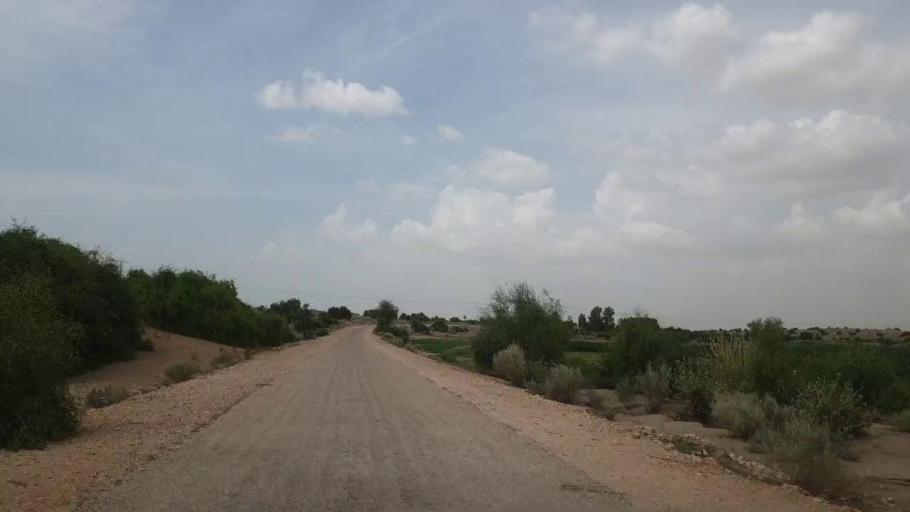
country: PK
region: Sindh
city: Kot Diji
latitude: 27.2127
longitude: 69.0832
